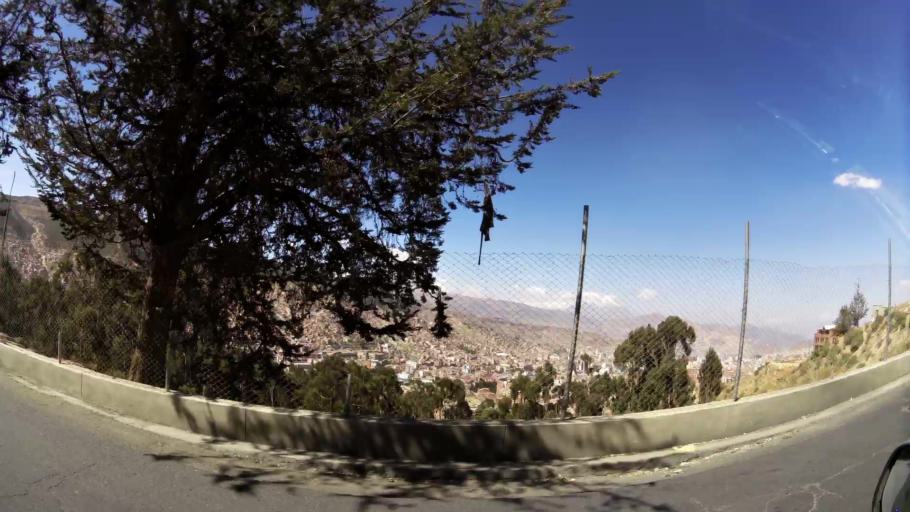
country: BO
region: La Paz
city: La Paz
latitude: -16.4862
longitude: -68.1551
